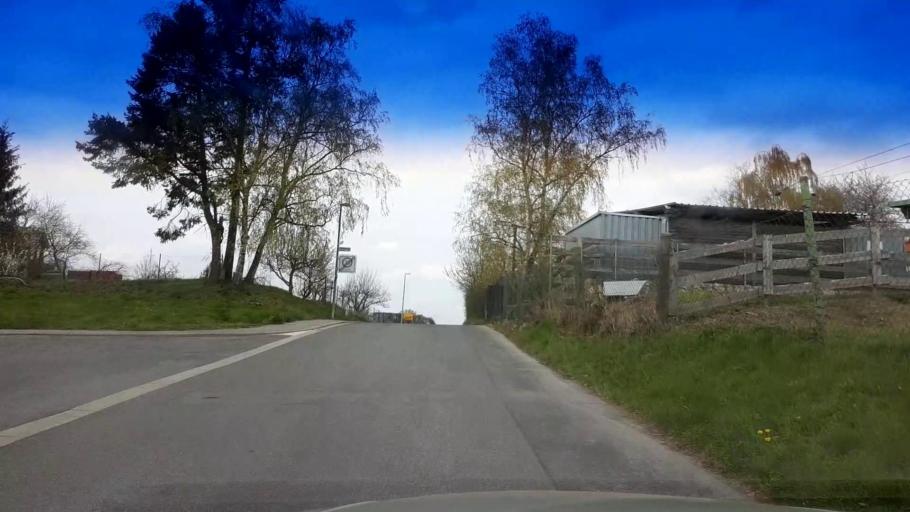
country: DE
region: Bavaria
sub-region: Upper Franconia
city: Bischberg
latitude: 49.9061
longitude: 10.8445
